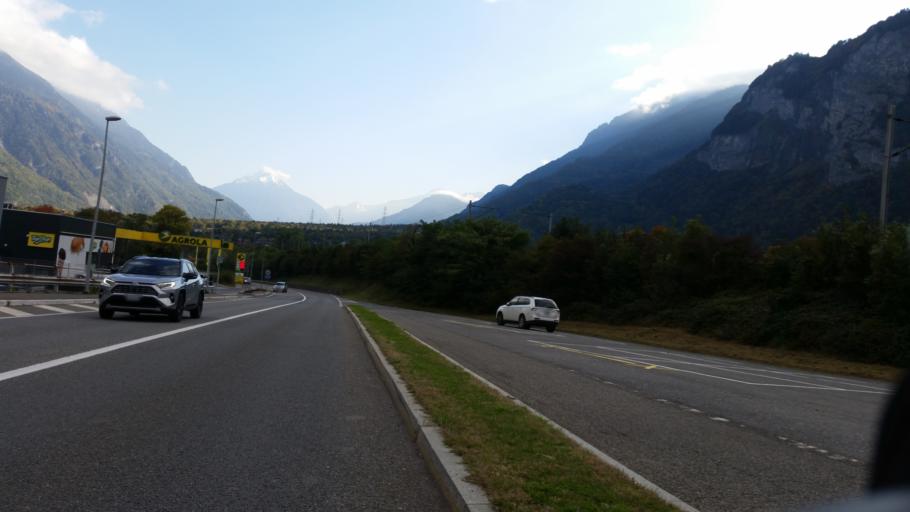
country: CH
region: Valais
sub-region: Saint-Maurice District
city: Saint-Maurice
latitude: 46.2077
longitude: 7.0070
